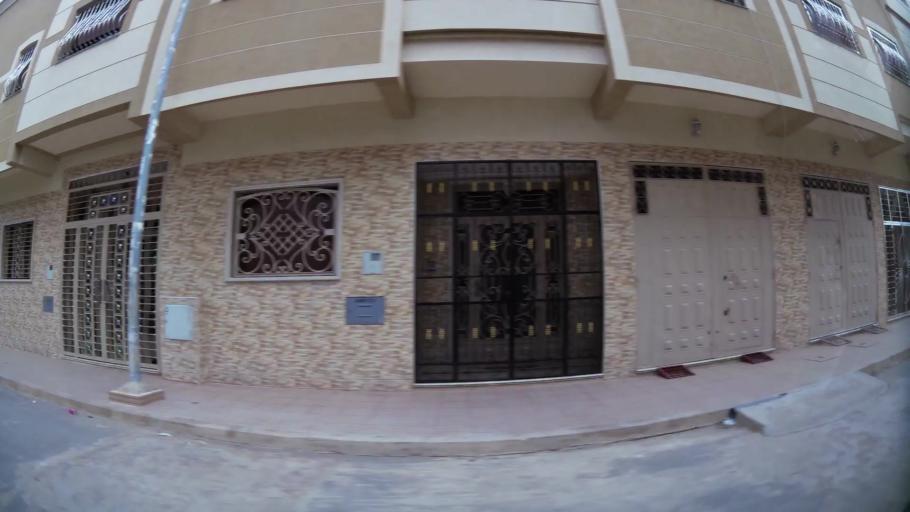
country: MA
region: Oriental
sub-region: Nador
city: Nador
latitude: 35.1635
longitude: -2.9350
